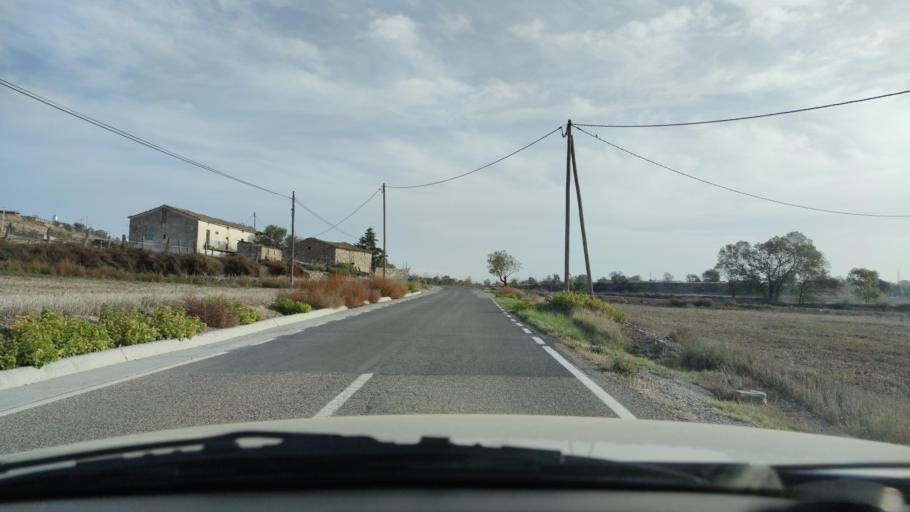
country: ES
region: Catalonia
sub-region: Provincia de Lleida
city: Cervera
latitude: 41.7398
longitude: 1.3037
